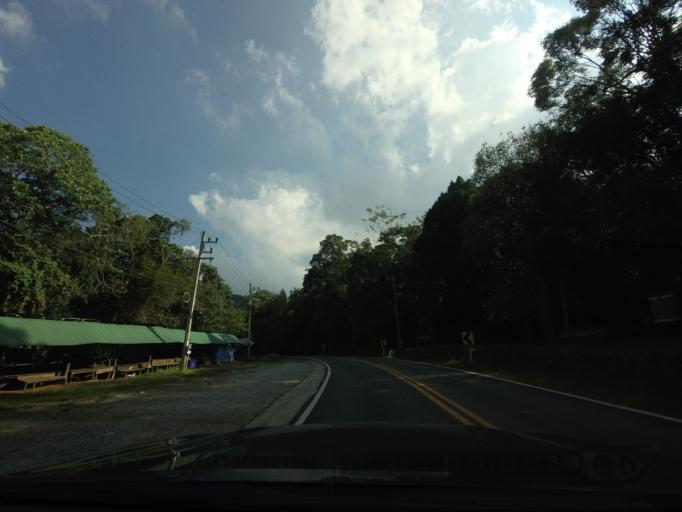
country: TH
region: Phitsanulok
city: Nakhon Thai
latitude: 16.9933
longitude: 101.0123
